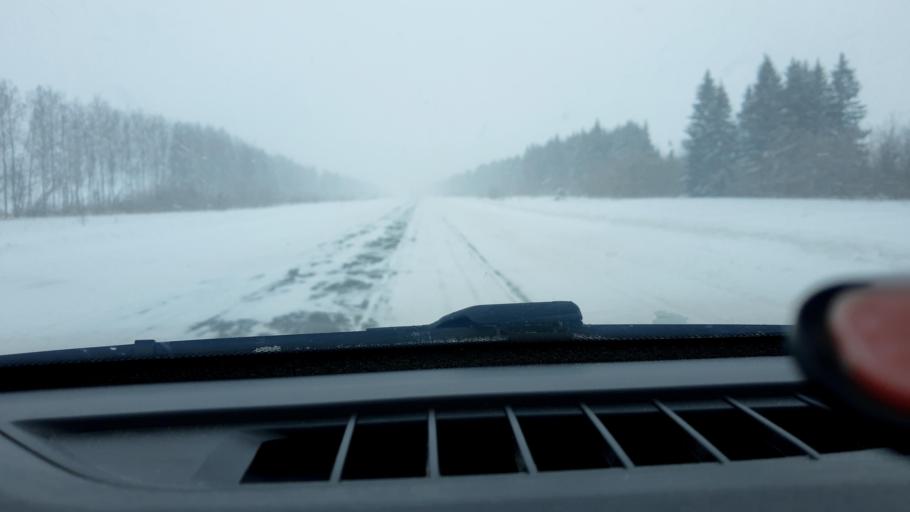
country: RU
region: Nizjnij Novgorod
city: Buturlino
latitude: 55.6352
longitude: 44.8464
